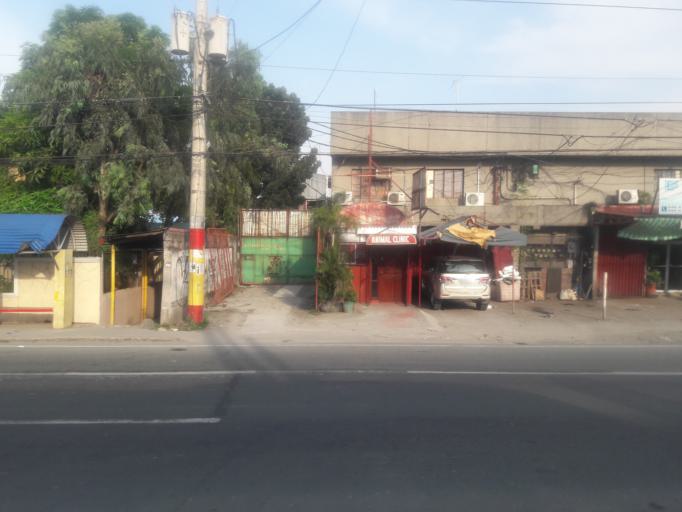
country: PH
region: Calabarzon
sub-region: Province of Cavite
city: Imus
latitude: 14.4018
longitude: 120.9403
